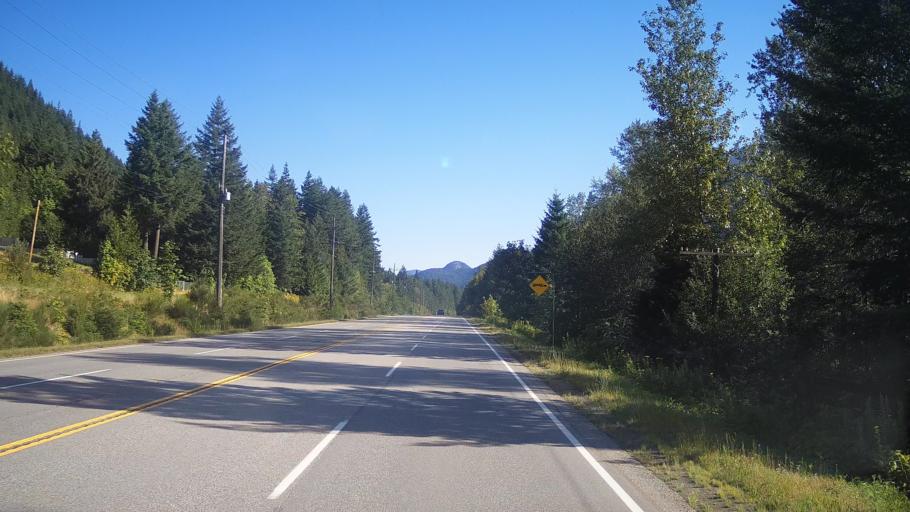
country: CA
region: British Columbia
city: Hope
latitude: 49.4951
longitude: -121.4204
